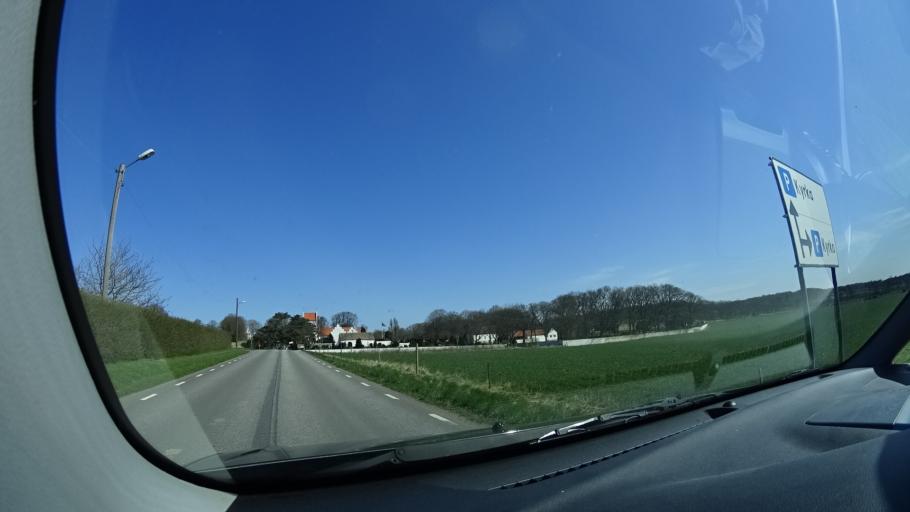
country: SE
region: Skane
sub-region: Hoganas Kommun
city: Hoganas
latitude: 56.2571
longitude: 12.5717
